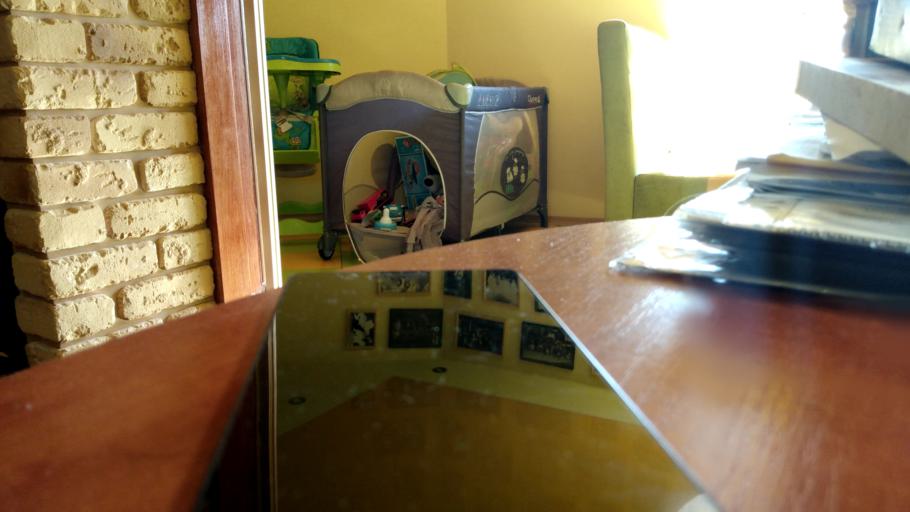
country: RU
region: Penza
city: Serdobsk
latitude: 52.4562
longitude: 44.2880
